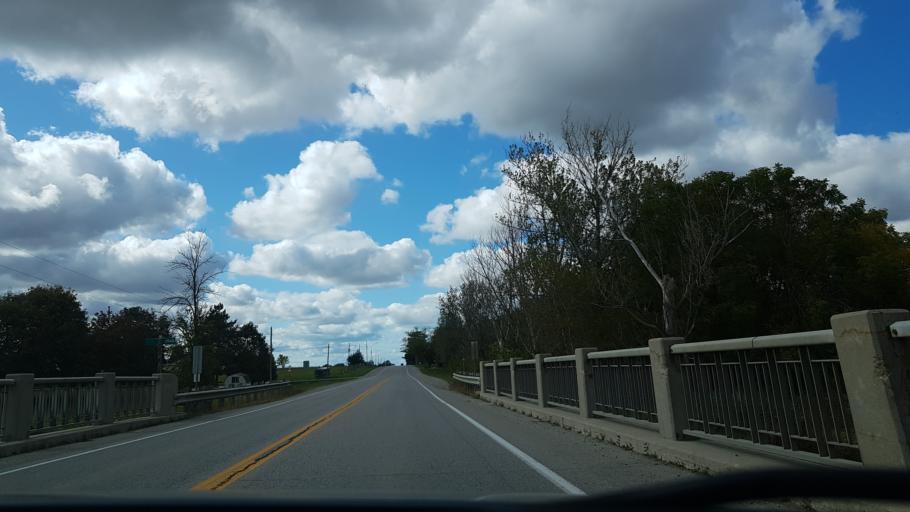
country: CA
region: Ontario
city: South Huron
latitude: 43.3602
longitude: -81.4987
